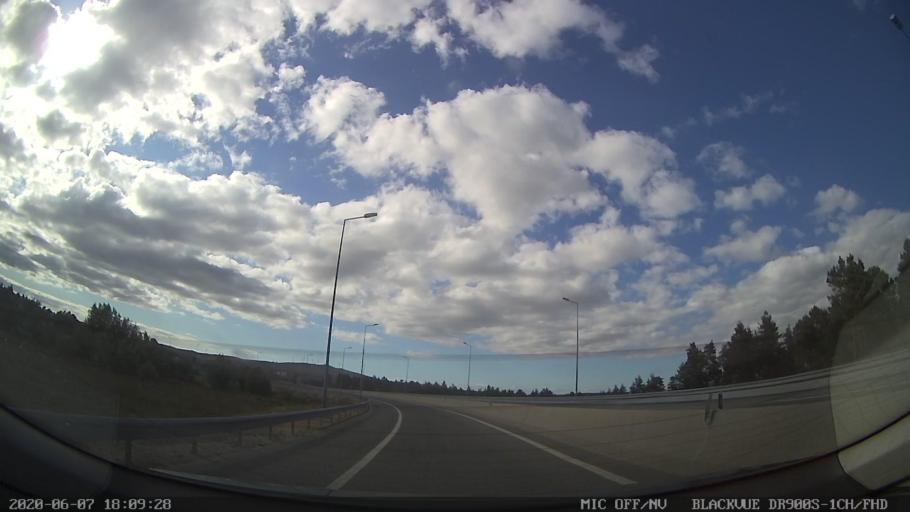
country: PT
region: Vila Real
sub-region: Vila Pouca de Aguiar
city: Vila Pouca de Aguiar
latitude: 41.5065
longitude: -7.6545
